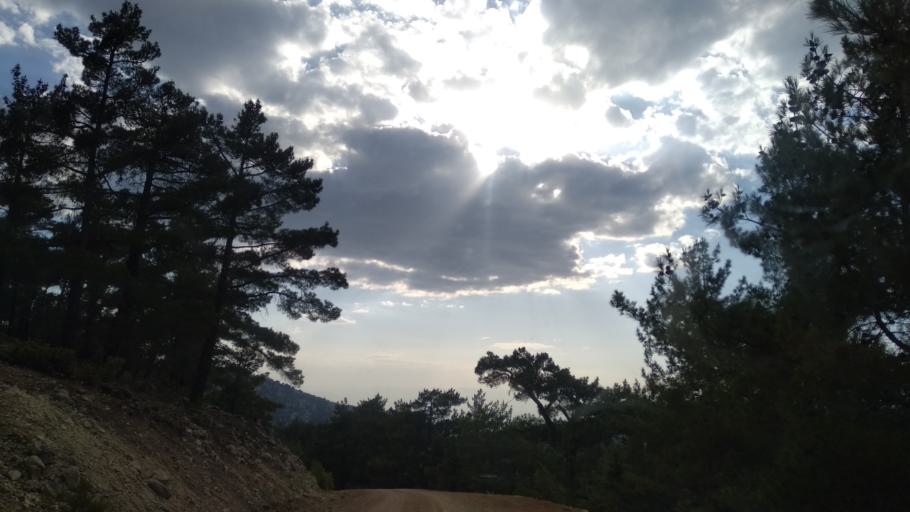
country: TR
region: Mersin
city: Sarikavak
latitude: 36.6004
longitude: 33.7162
